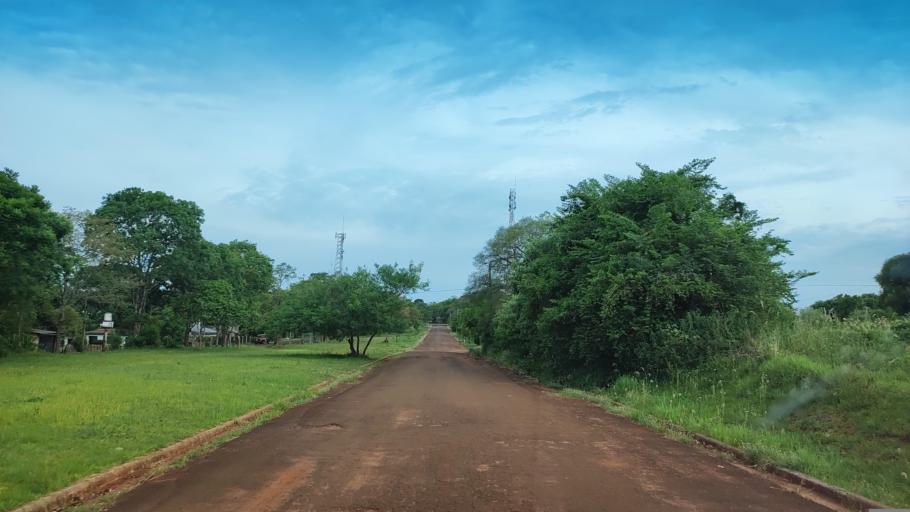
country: AR
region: Misiones
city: Gobernador Roca
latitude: -27.1267
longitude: -55.5143
